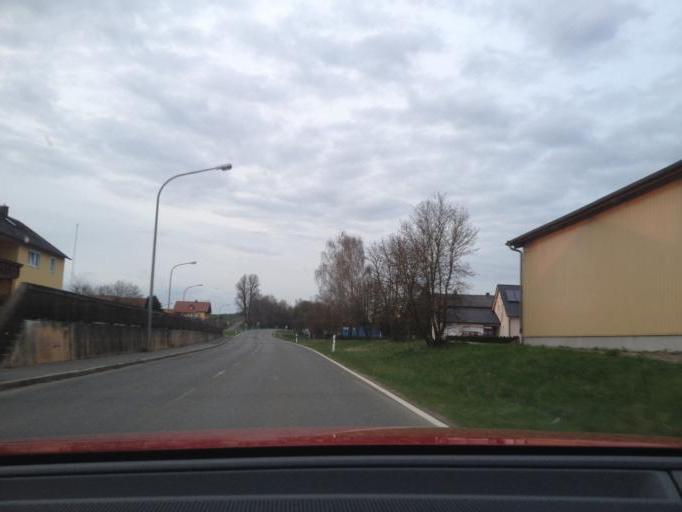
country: DE
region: Bavaria
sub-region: Upper Palatinate
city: Speinshart
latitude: 49.7767
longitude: 11.8142
